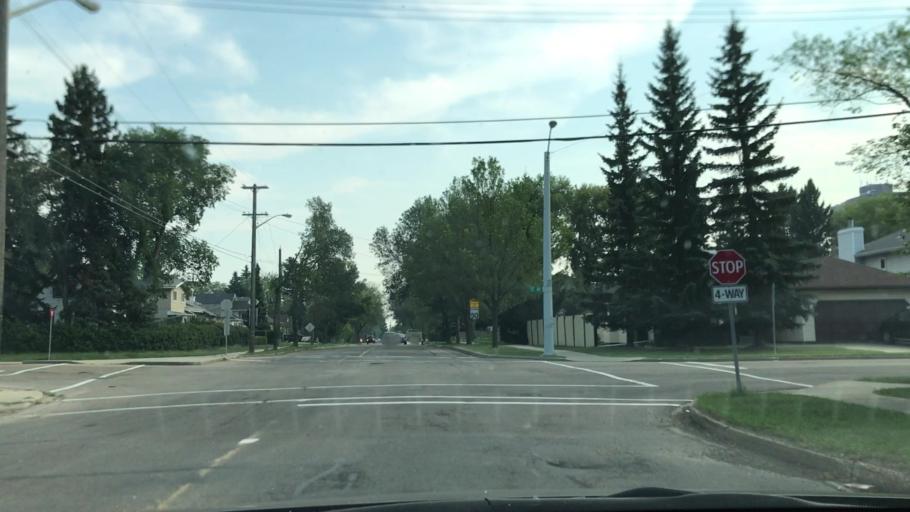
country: CA
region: Alberta
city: Edmonton
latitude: 53.4944
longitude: -113.5119
